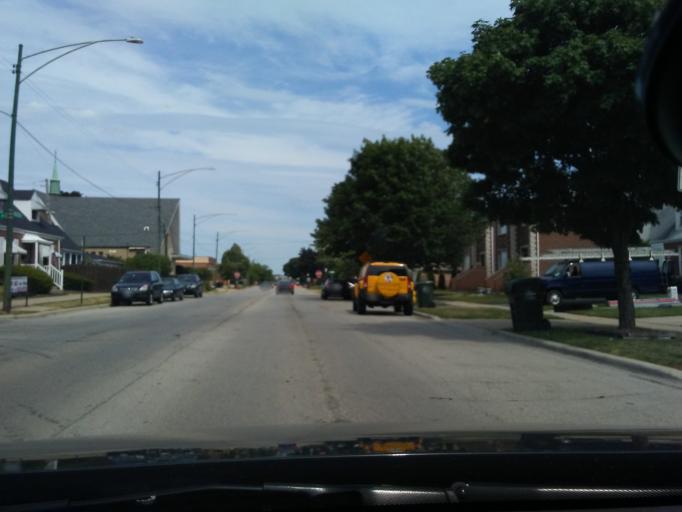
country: US
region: Illinois
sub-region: Cook County
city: Harwood Heights
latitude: 41.9744
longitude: -87.8133
